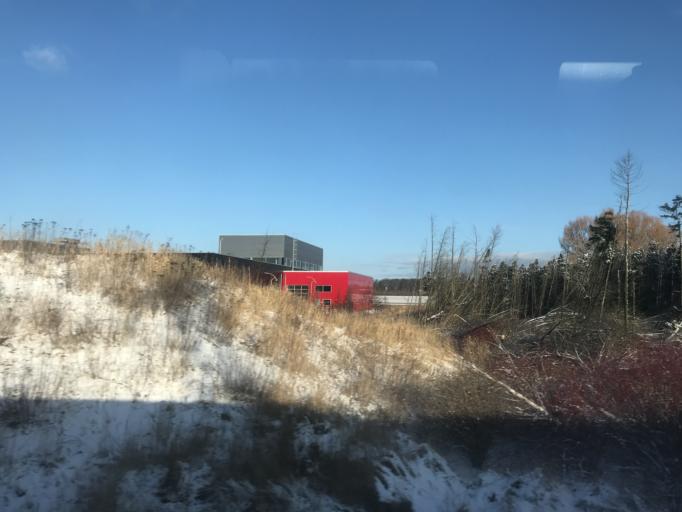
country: SE
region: Skane
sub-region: Burlovs Kommun
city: Arloev
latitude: 55.6480
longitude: 13.0923
